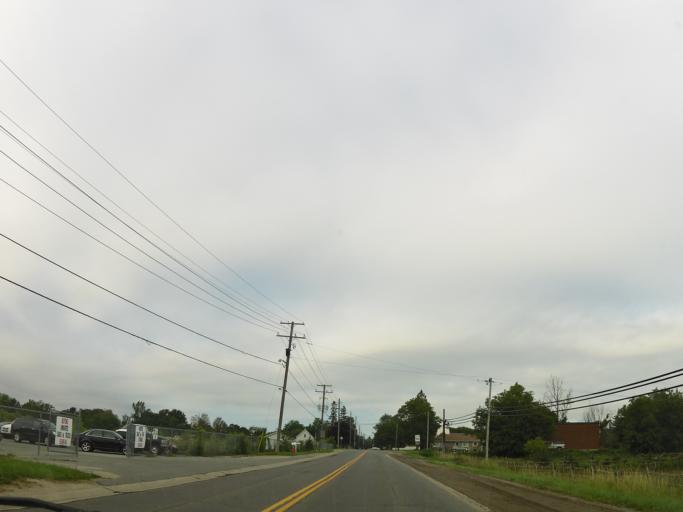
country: CA
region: Ontario
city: Kingston
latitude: 44.4058
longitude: -76.6601
